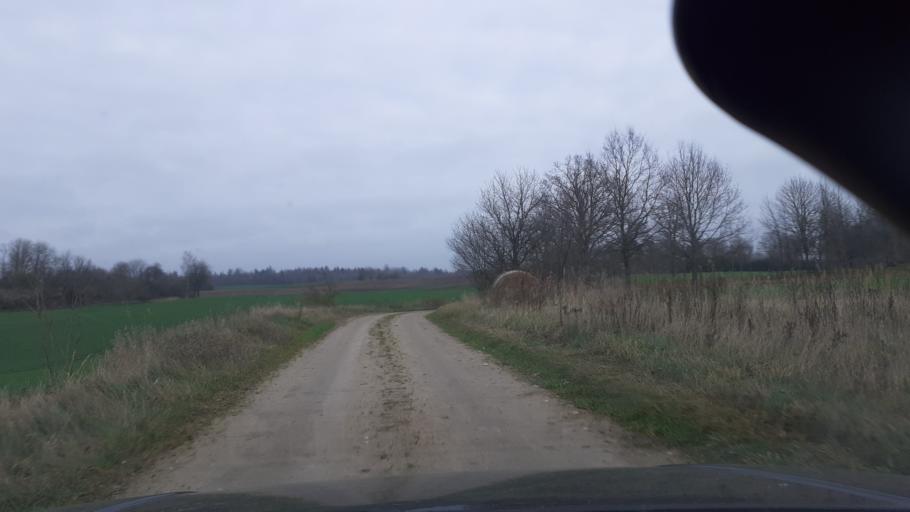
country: LV
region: Aizpute
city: Aizpute
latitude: 56.7866
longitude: 21.7603
